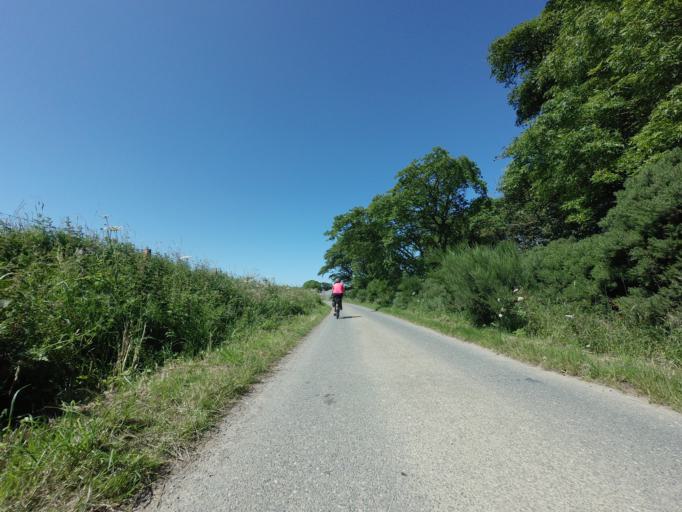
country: GB
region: Scotland
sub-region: Aberdeenshire
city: Macduff
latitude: 57.6410
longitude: -2.5009
